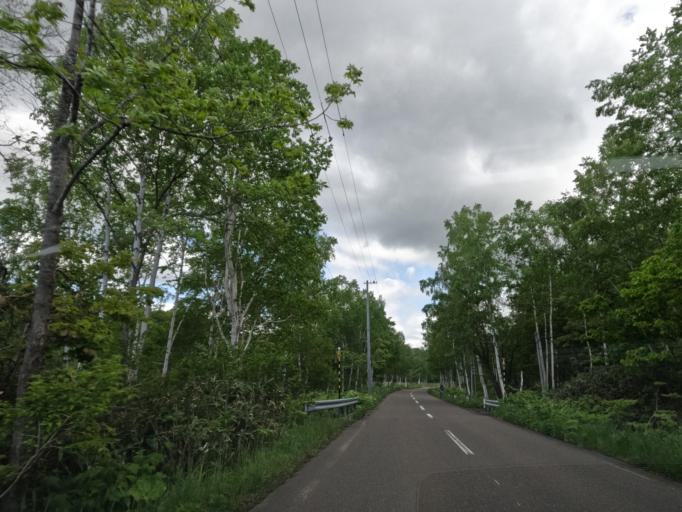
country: JP
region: Hokkaido
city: Tobetsu
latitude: 43.4562
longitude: 141.5917
